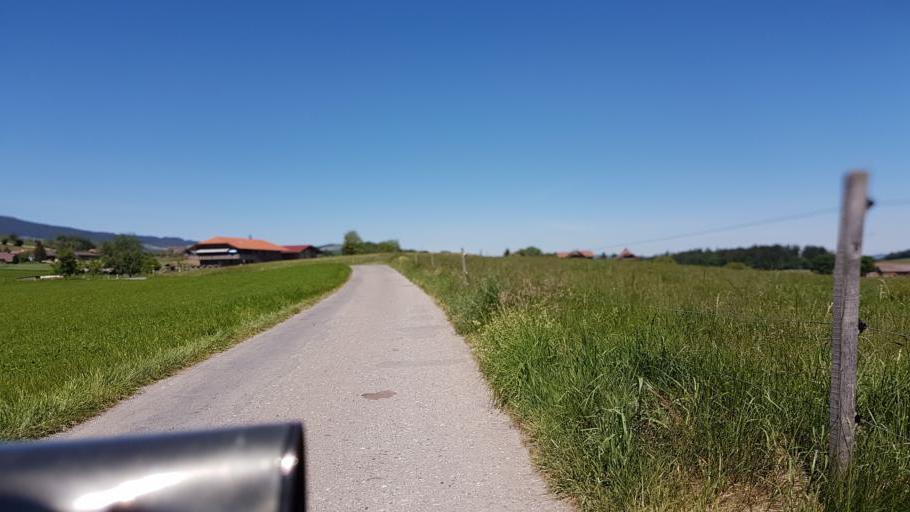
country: CH
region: Bern
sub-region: Thun District
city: Thierachern
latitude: 46.7385
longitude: 7.5626
